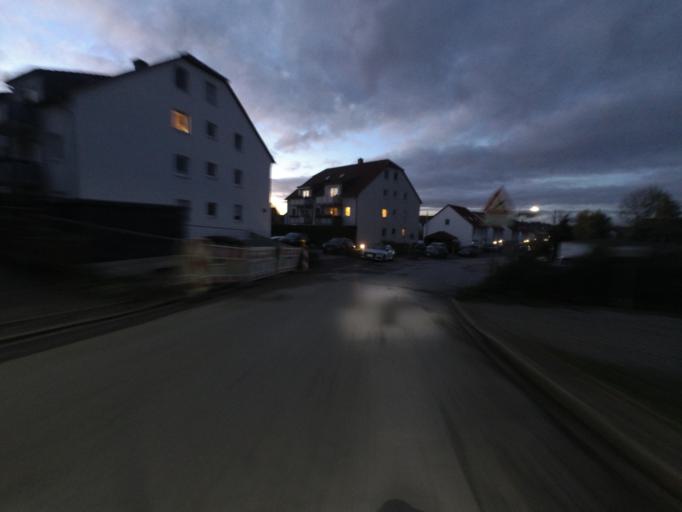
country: DE
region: North Rhine-Westphalia
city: Sprockhovel
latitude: 51.3580
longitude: 7.2470
